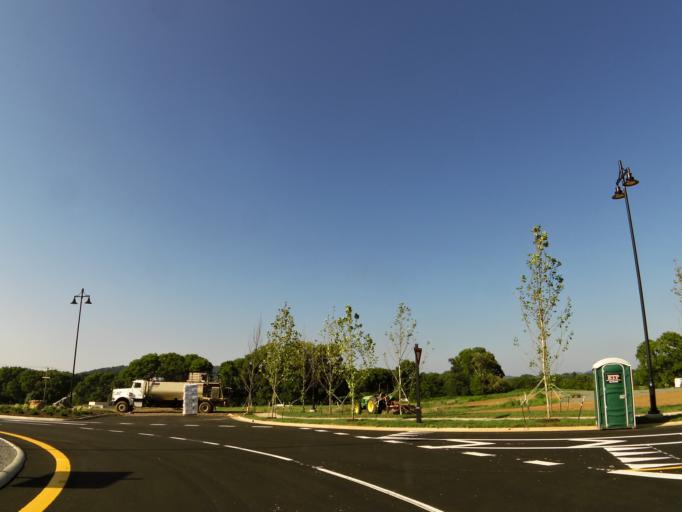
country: US
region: Tennessee
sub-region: Blount County
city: Eagleton Village
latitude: 35.8005
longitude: -83.9340
